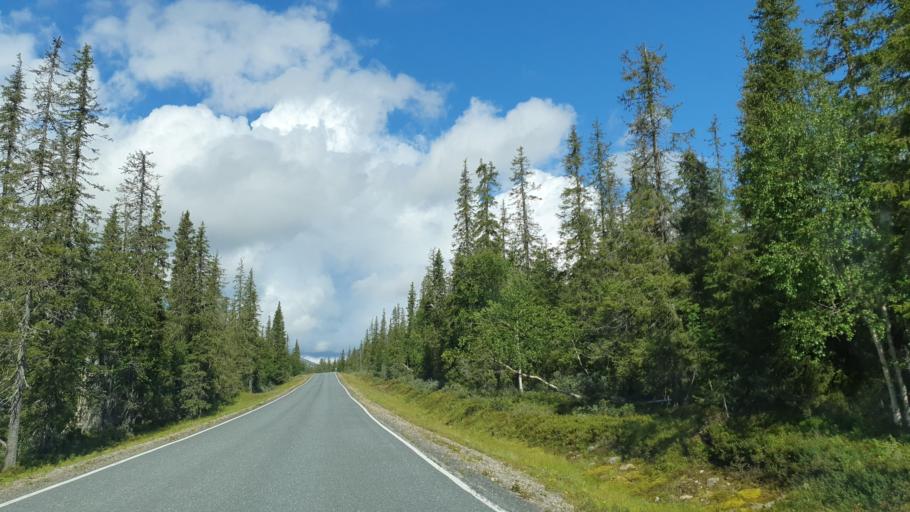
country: FI
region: Lapland
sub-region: Tunturi-Lappi
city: Muonio
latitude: 68.0387
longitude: 24.0663
